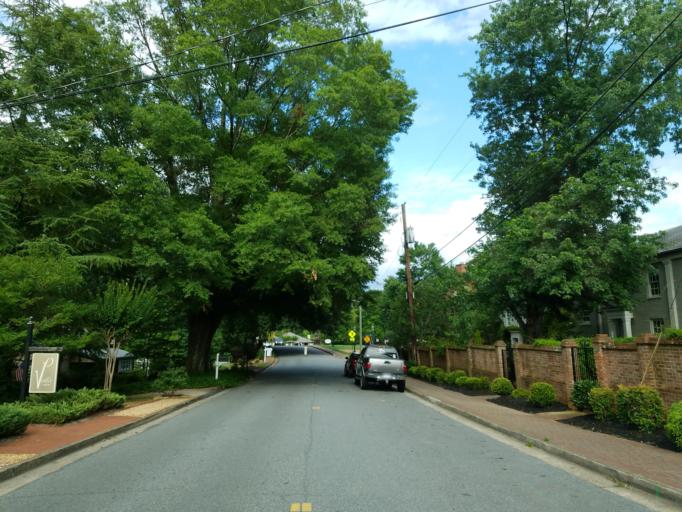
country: US
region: Georgia
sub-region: Fulton County
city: Roswell
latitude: 34.0154
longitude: -84.3609
